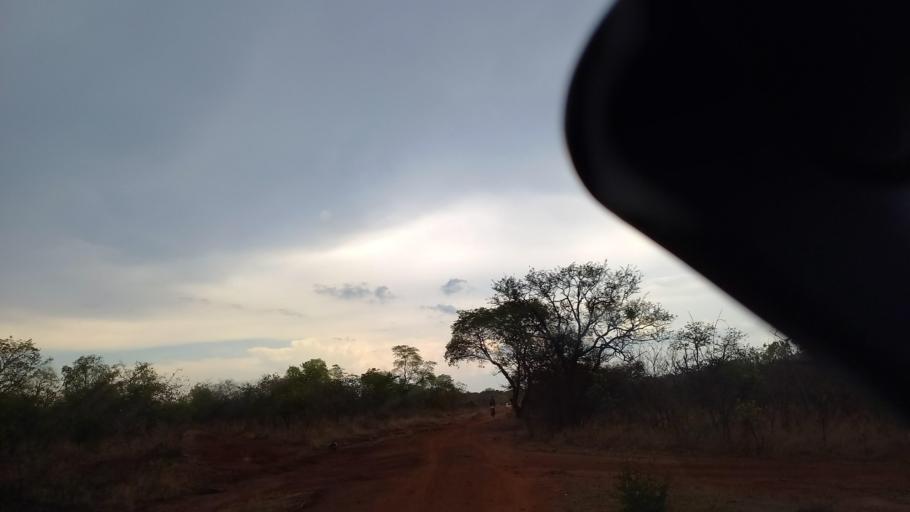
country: ZM
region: Lusaka
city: Kafue
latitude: -15.9978
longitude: 28.2777
